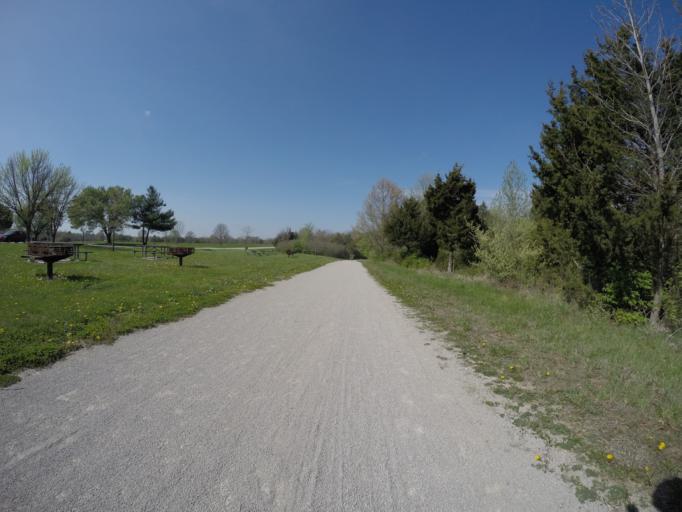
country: US
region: Missouri
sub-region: Jackson County
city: Grandview
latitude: 38.8956
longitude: -94.4900
